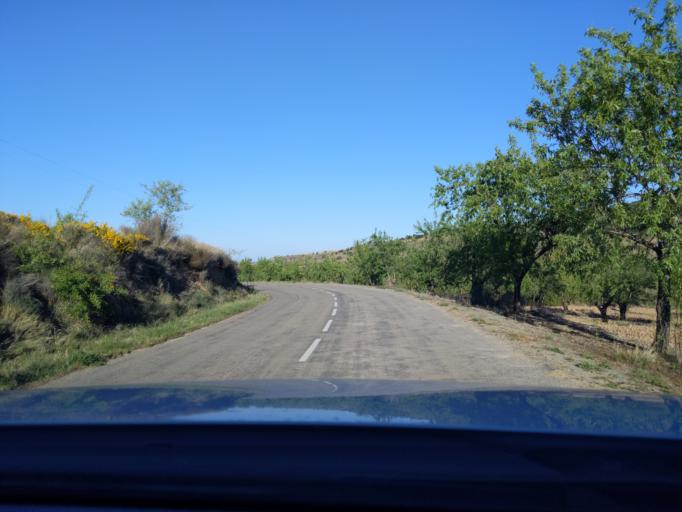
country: ES
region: La Rioja
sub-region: Provincia de La Rioja
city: Bergasa
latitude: 42.2461
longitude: -2.1394
